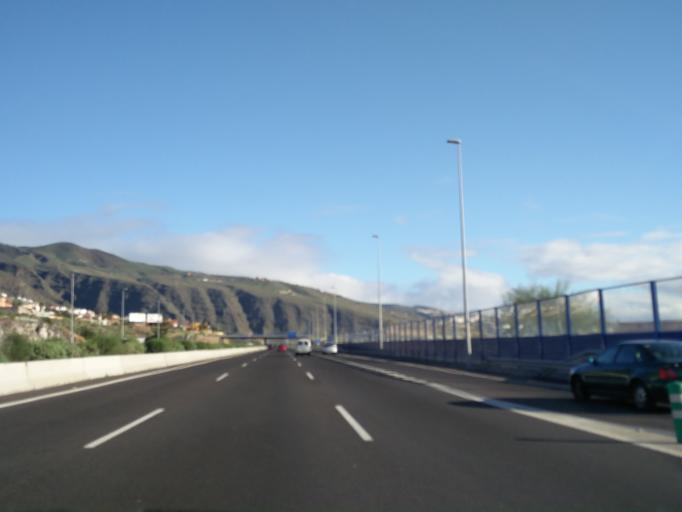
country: ES
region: Canary Islands
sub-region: Provincia de Santa Cruz de Tenerife
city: Candelaria
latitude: 28.3606
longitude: -16.3715
